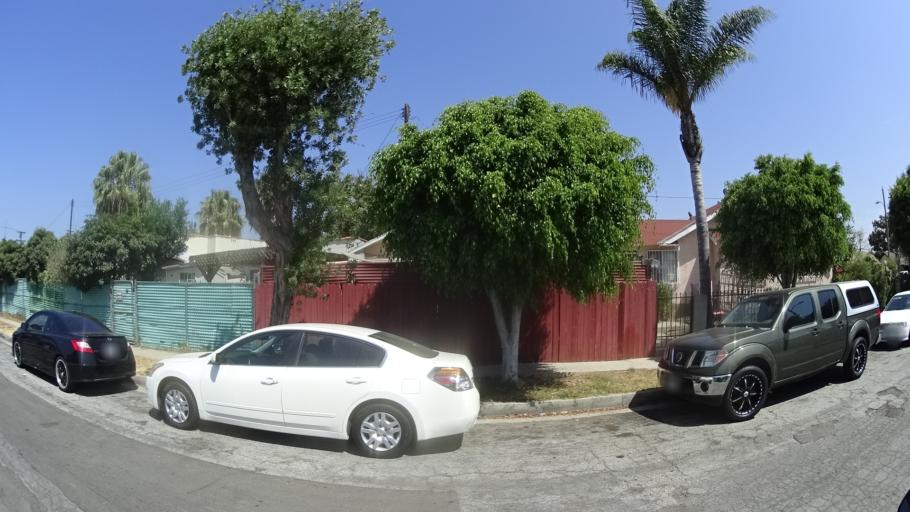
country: US
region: California
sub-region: Los Angeles County
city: View Park-Windsor Hills
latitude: 33.9805
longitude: -118.3398
